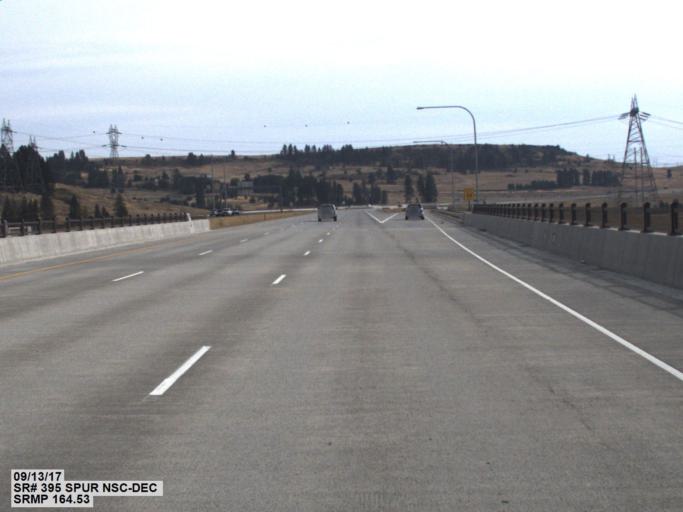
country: US
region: Washington
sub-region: Spokane County
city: Mead
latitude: 47.7569
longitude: -117.3633
